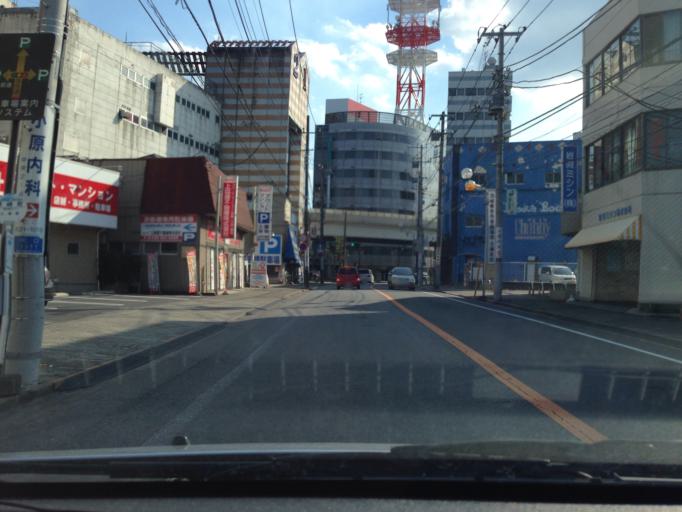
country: JP
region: Ibaraki
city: Naka
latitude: 36.0820
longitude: 140.2028
